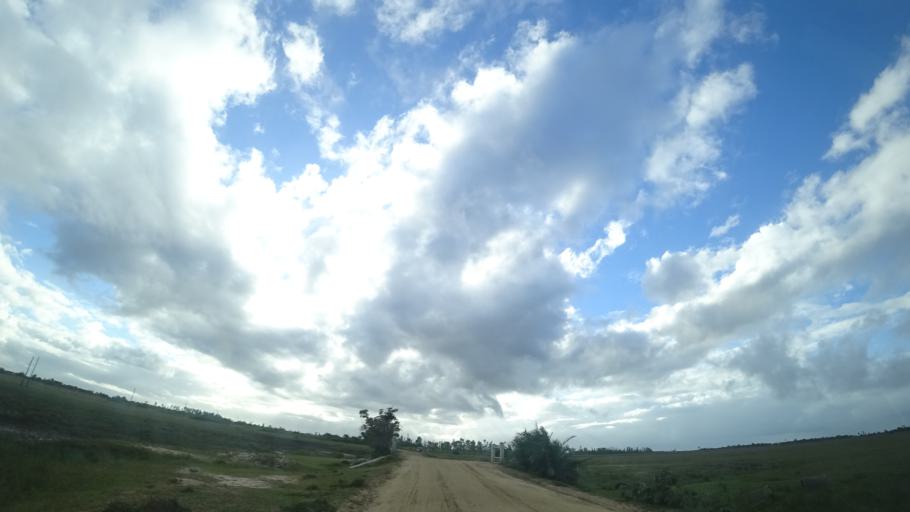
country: MZ
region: Sofala
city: Beira
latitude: -19.7275
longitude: 34.9877
